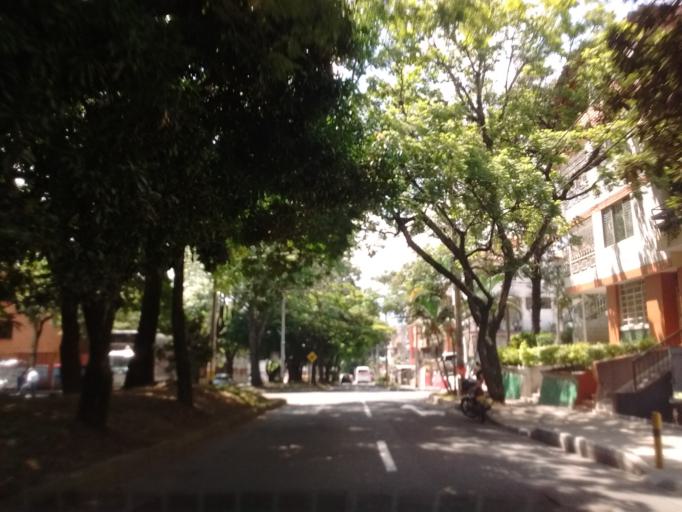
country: CO
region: Antioquia
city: Medellin
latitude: 6.2436
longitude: -75.6045
